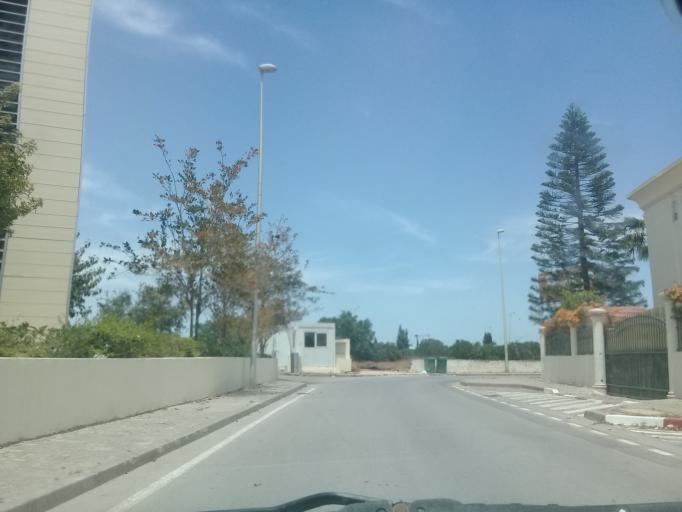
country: TN
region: Ariana
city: Ariana
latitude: 36.8353
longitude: 10.2273
